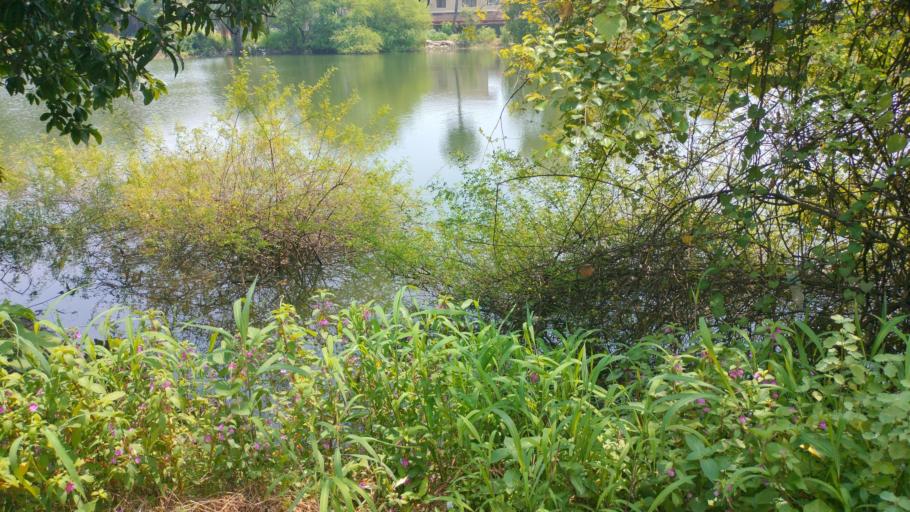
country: IN
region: Maharashtra
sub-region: Thane
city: Virar
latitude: 19.3913
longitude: 72.7823
